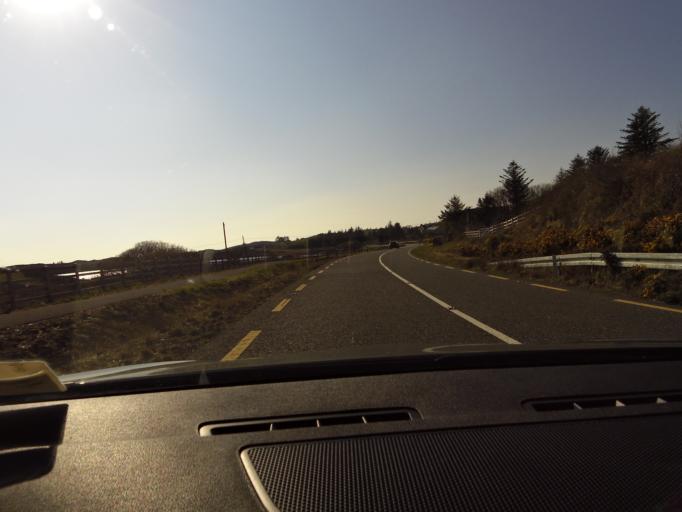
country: IE
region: Connaught
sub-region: County Galway
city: Clifden
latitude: 53.4833
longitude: -9.9528
